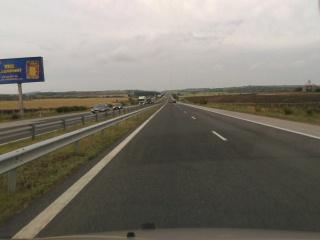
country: BG
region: Stara Zagora
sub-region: Obshtina Chirpan
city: Chirpan
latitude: 42.2098
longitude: 25.3076
